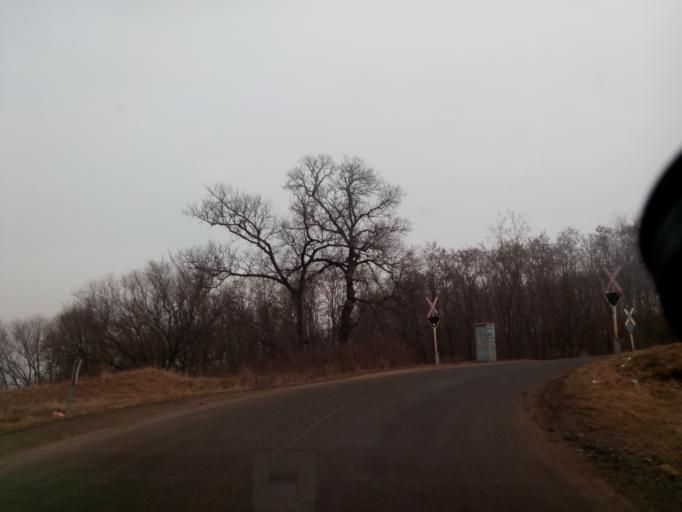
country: HU
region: Borsod-Abauj-Zemplen
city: Gonc
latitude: 48.4787
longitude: 21.2580
